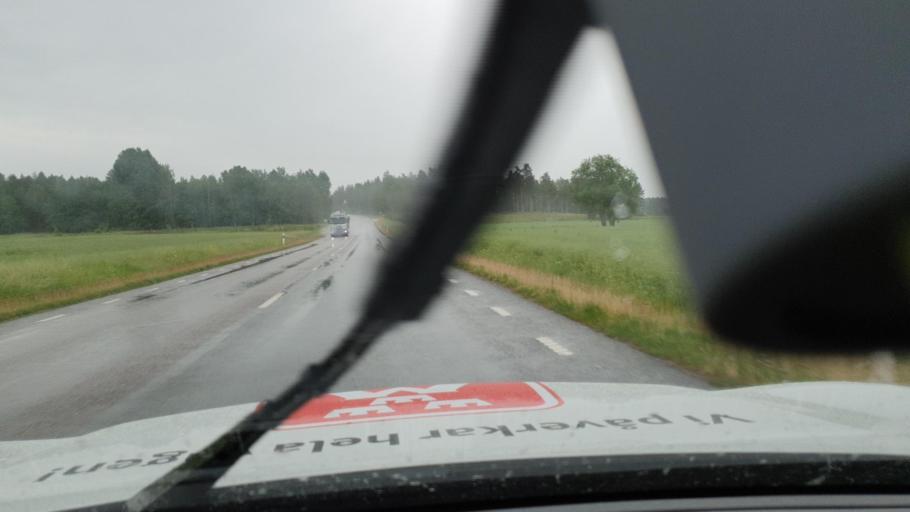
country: SE
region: Vaestra Goetaland
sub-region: Mariestads Kommun
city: Mariestad
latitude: 58.7916
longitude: 13.9664
